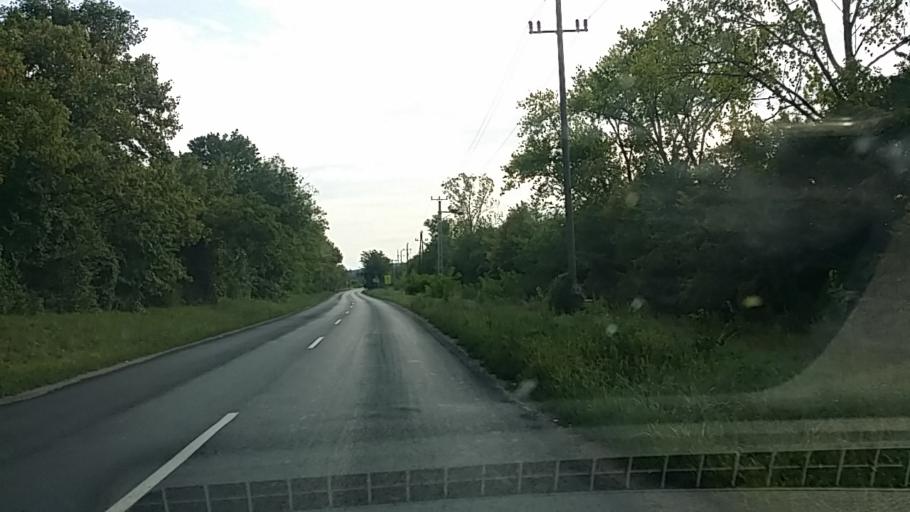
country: HU
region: Gyor-Moson-Sopron
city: Fertorakos
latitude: 47.7178
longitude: 16.6160
